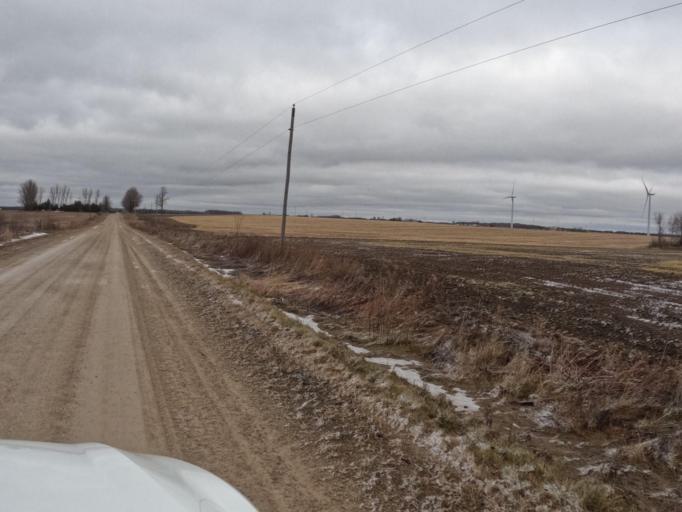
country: CA
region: Ontario
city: Shelburne
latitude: 44.0269
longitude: -80.3704
